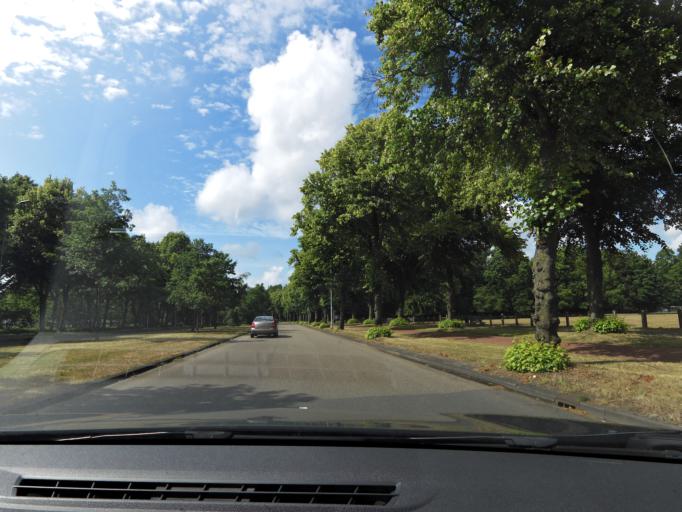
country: NL
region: South Holland
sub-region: Gemeente Rijswijk
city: Rijswijk
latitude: 52.0397
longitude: 4.2996
